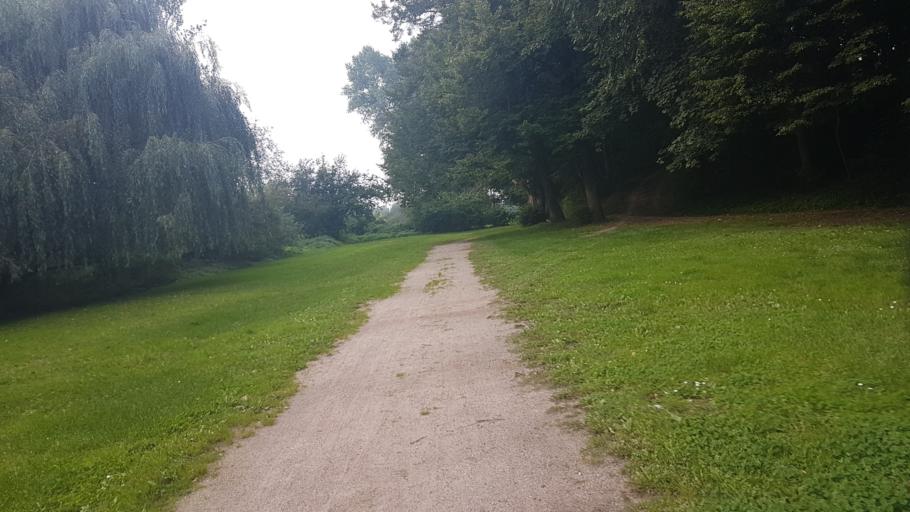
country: DE
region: Mecklenburg-Vorpommern
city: Garz
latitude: 54.3129
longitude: 13.3469
